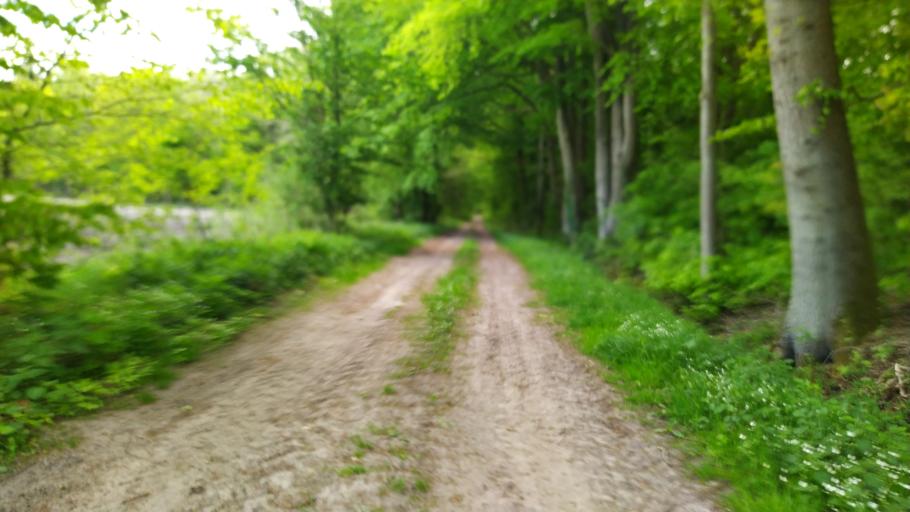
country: DE
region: Lower Saxony
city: Brest
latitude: 53.4186
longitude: 9.3822
